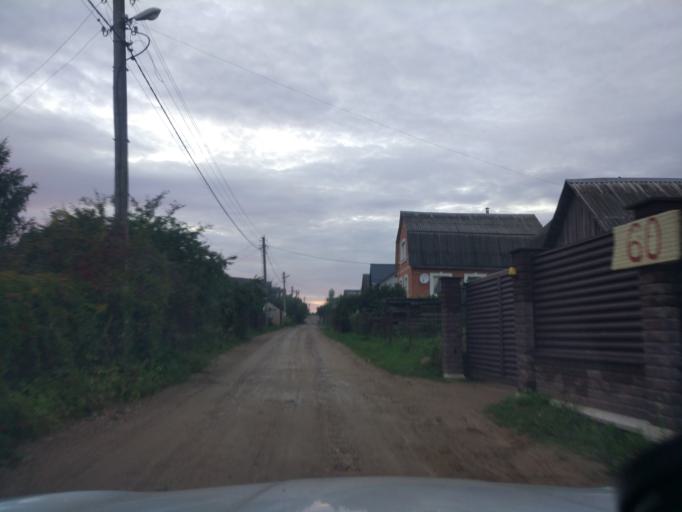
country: BY
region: Minsk
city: Astrashytski Haradok
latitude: 54.0873
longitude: 27.6993
